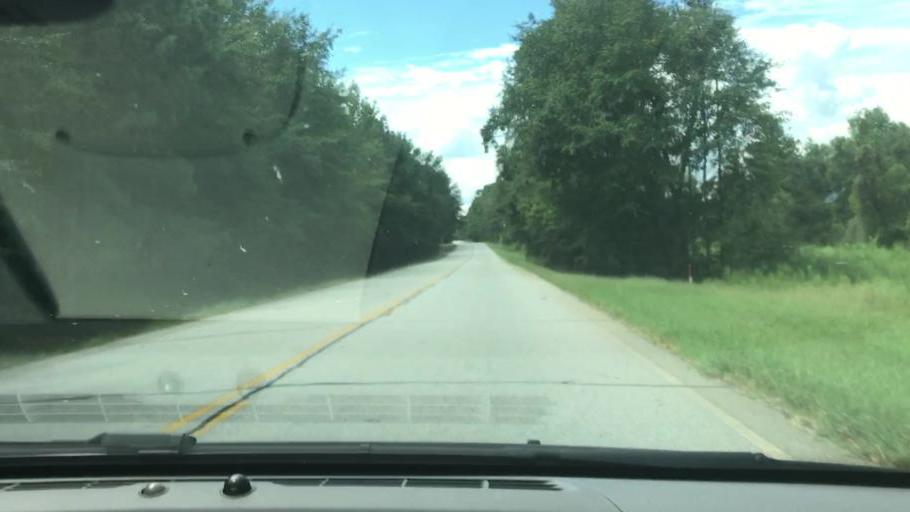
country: US
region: Georgia
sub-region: Stewart County
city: Lumpkin
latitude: 32.1455
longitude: -84.8341
